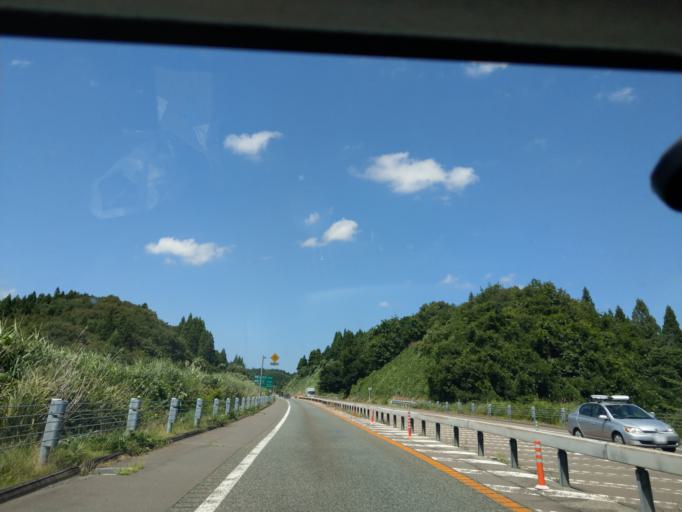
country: JP
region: Akita
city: Akita
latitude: 39.6703
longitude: 140.1881
